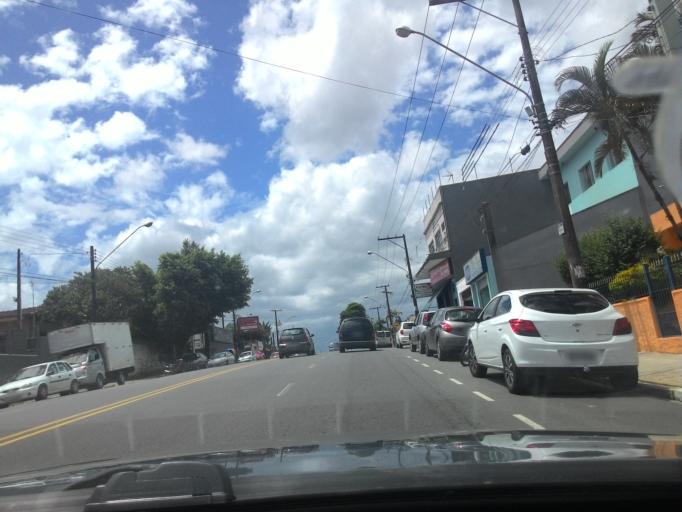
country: BR
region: Sao Paulo
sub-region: Registro
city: Registro
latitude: -24.5012
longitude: -47.8410
